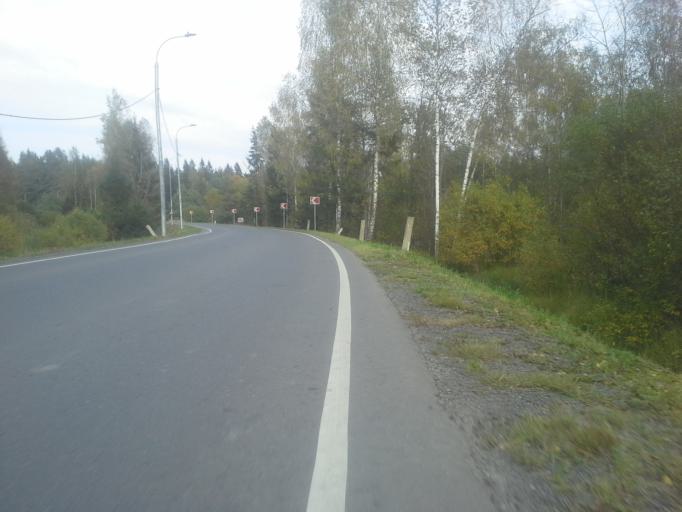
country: RU
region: Moskovskaya
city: Kievskij
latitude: 55.4106
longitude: 36.9430
